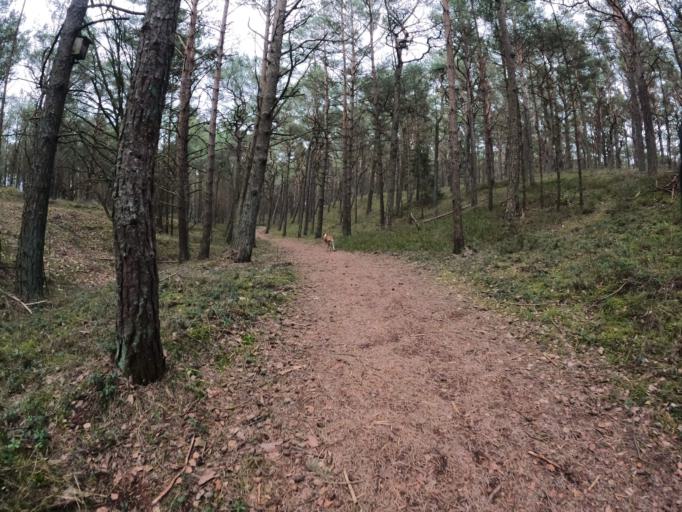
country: PL
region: West Pomeranian Voivodeship
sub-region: Powiat gryficki
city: Mrzezyno
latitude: 54.1390
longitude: 15.2667
